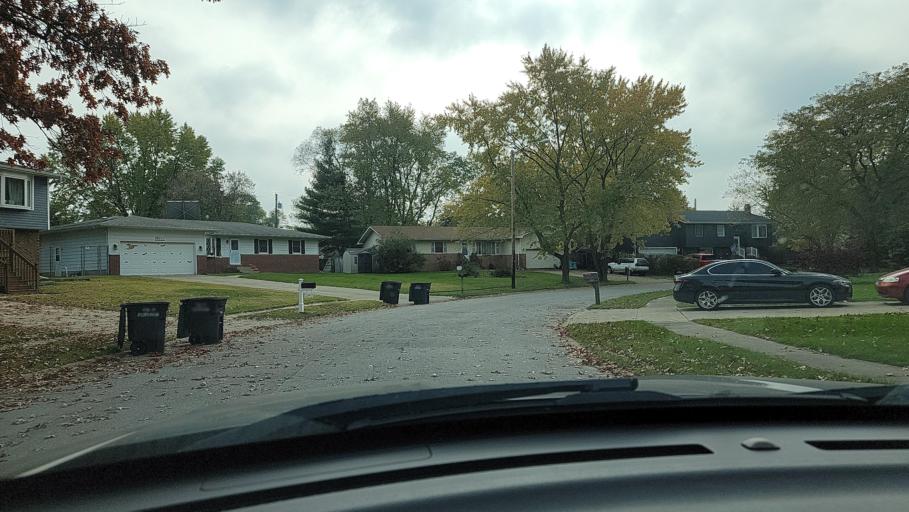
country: US
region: Indiana
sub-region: Porter County
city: Portage
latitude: 41.5920
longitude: -87.1591
